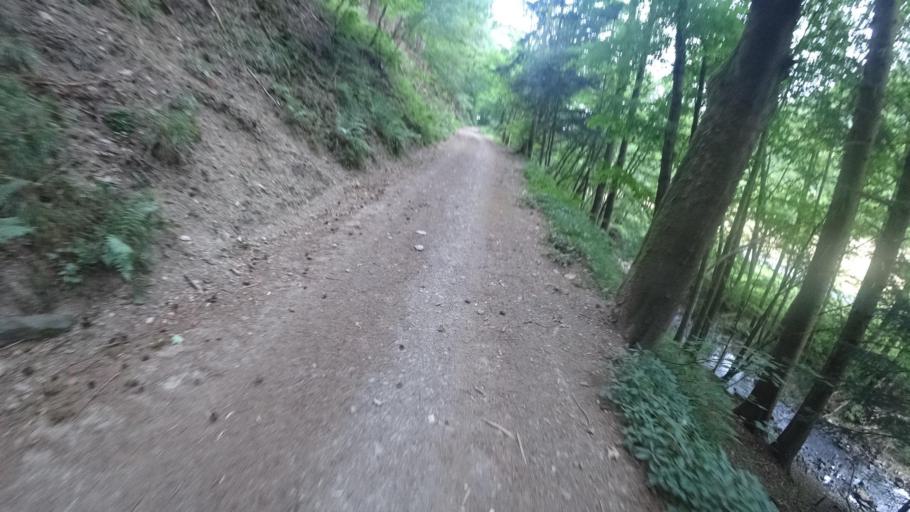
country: DE
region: Rheinland-Pfalz
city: Kesseling
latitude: 50.4828
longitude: 7.0015
